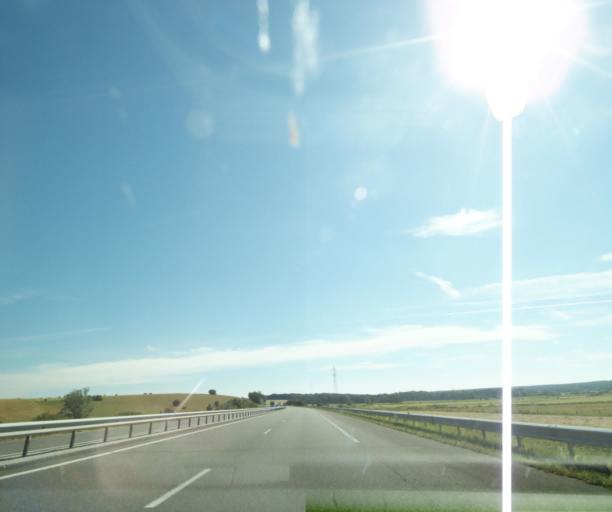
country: FR
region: Lorraine
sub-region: Departement des Vosges
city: Bulgneville
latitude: 48.1932
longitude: 5.7752
